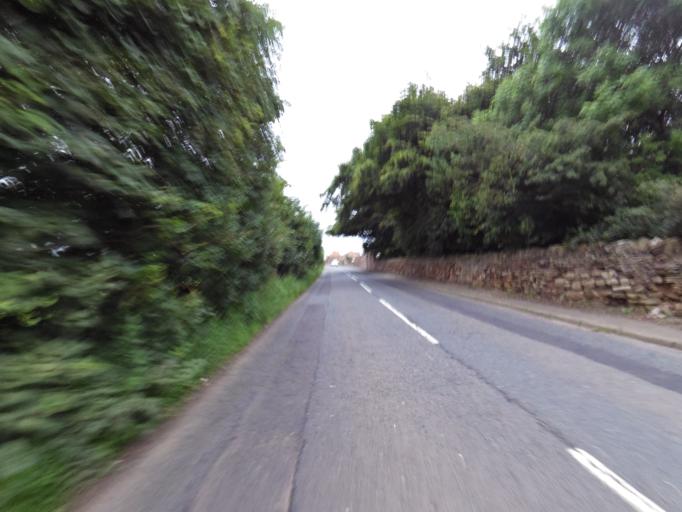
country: GB
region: Scotland
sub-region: Midlothian
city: Dalkeith
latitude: 55.9210
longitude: -3.0692
